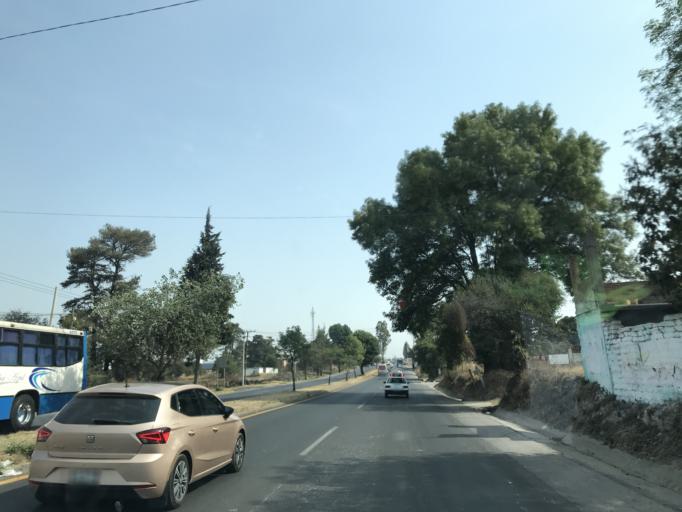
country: MX
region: Tlaxcala
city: Xiloxoxtla
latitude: 19.2605
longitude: -98.2001
